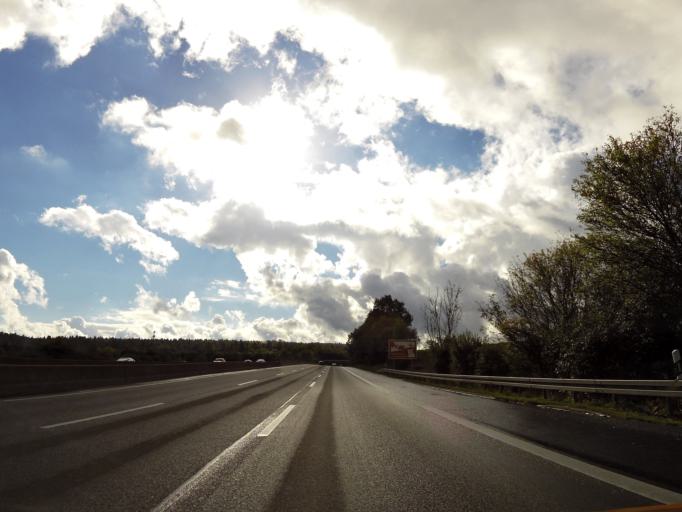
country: DE
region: Hesse
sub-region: Regierungsbezirk Kassel
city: Malsfeld
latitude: 51.0264
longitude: 9.4860
